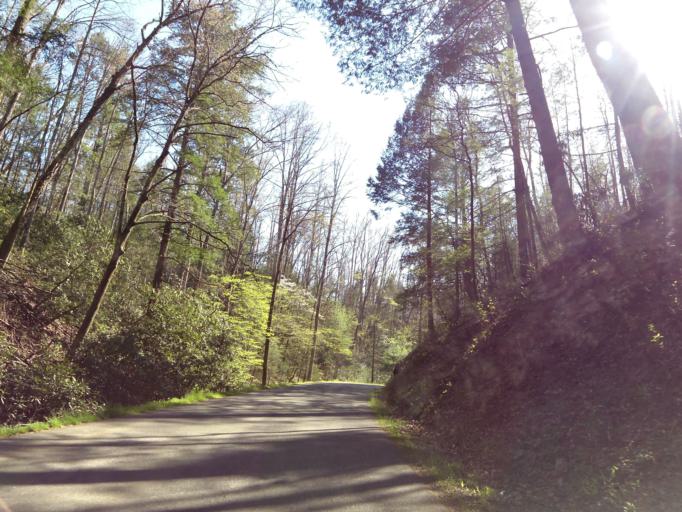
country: US
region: Tennessee
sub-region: Sevier County
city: Gatlinburg
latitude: 35.6826
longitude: -83.6464
